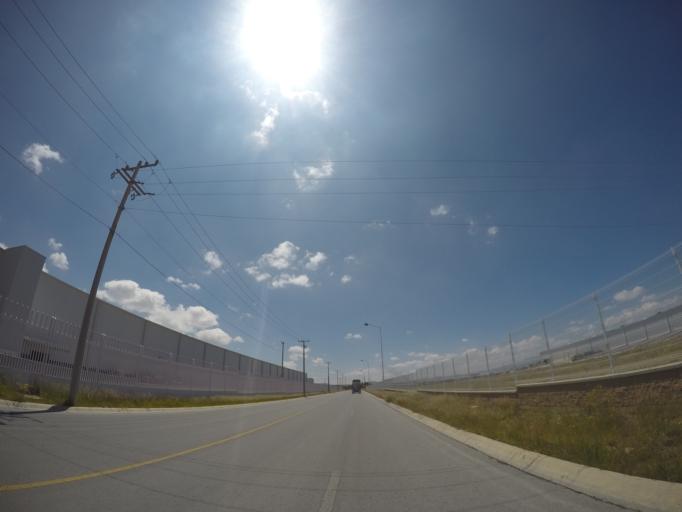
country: MX
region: San Luis Potosi
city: La Pila
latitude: 21.9703
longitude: -100.8750
